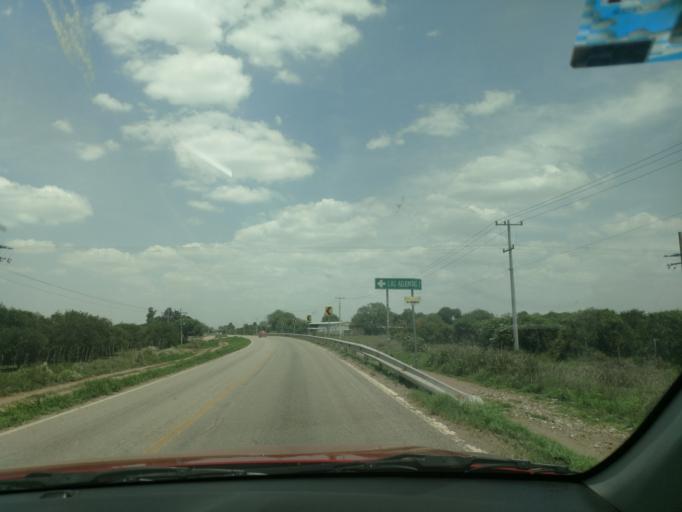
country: MX
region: San Luis Potosi
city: Ciudad Fernandez
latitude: 21.9510
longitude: -100.0642
